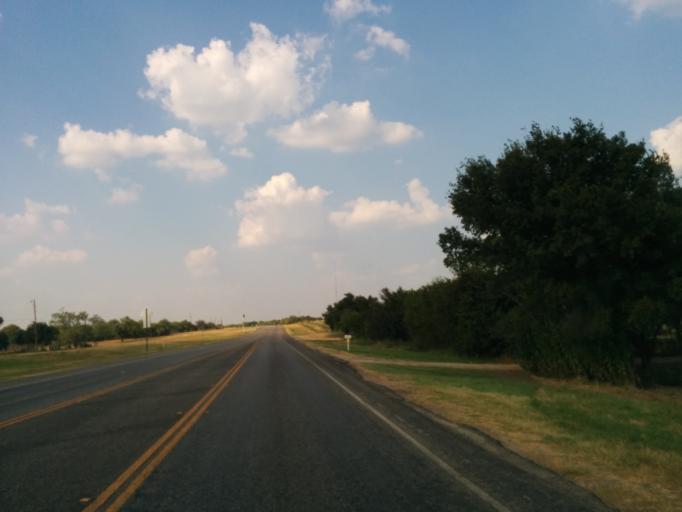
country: US
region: Texas
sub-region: Bexar County
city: Saint Hedwig
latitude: 29.3290
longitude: -98.2583
